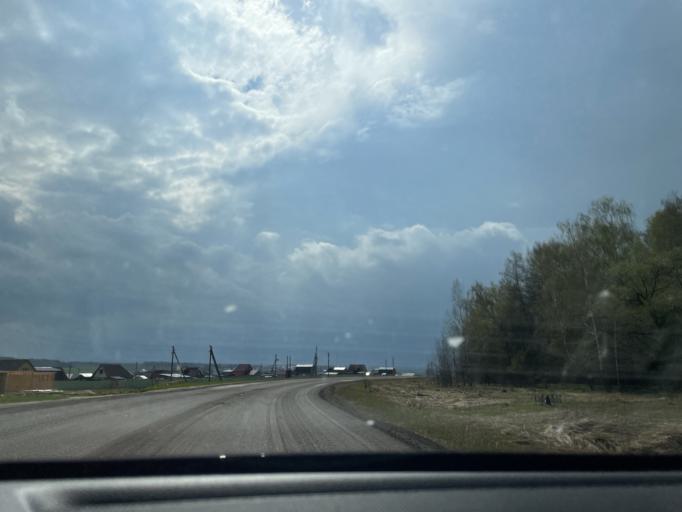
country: RU
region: Tula
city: Zaokskiy
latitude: 54.5857
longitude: 37.4962
